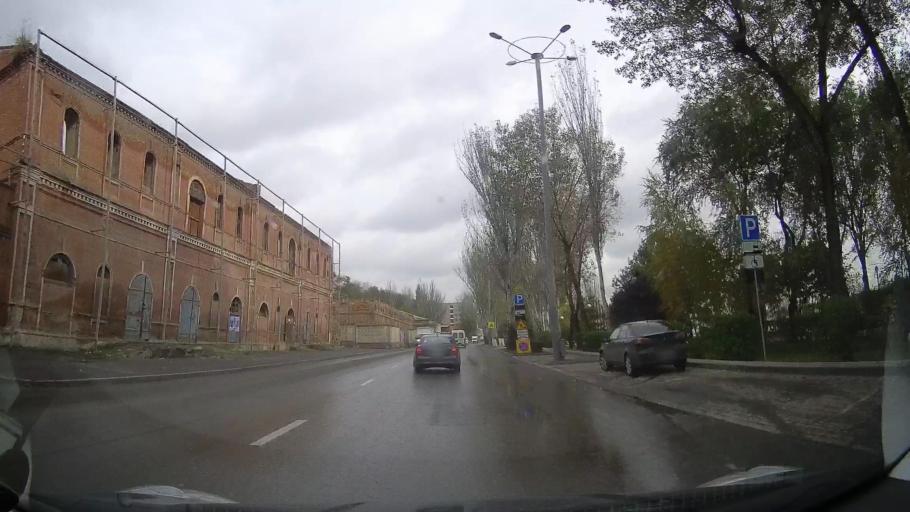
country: RU
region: Rostov
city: Rostov-na-Donu
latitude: 47.2172
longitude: 39.7256
